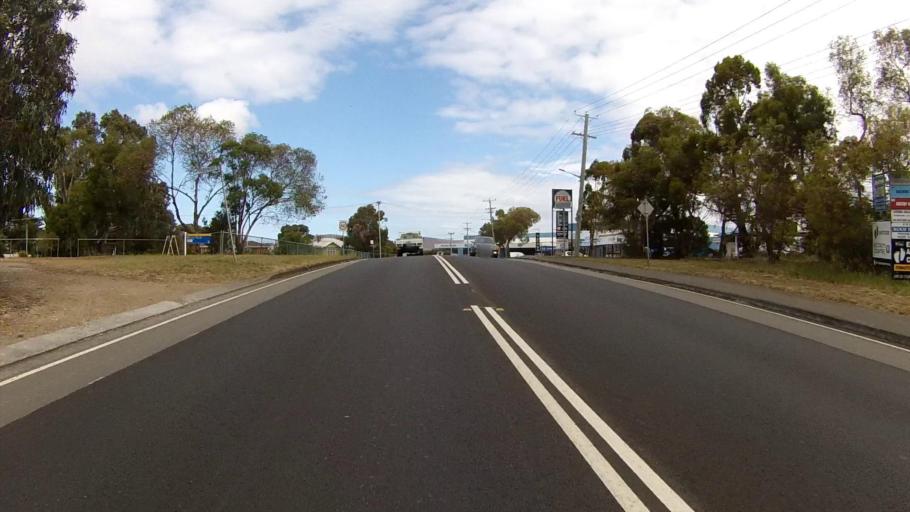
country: AU
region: Tasmania
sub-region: Clarence
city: Rokeby
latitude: -42.8998
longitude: 147.4443
